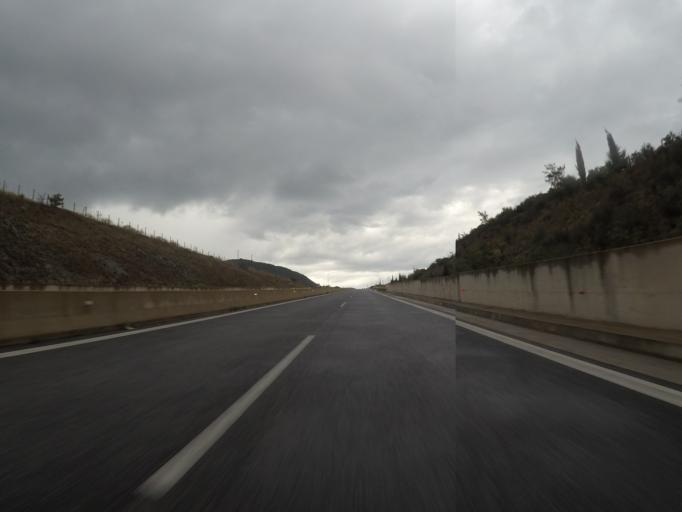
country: GR
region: Peloponnese
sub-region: Nomos Arkadias
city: Megalopoli
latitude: 37.3285
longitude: 22.0657
